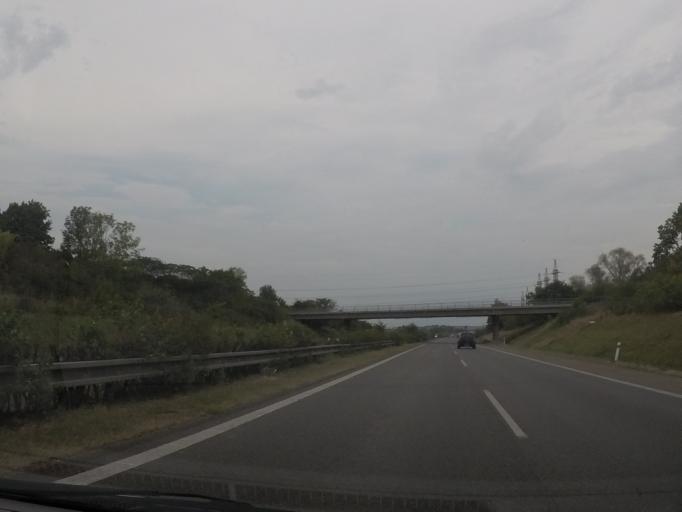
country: SK
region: Bratislavsky
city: Stupava
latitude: 48.2859
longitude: 17.0099
